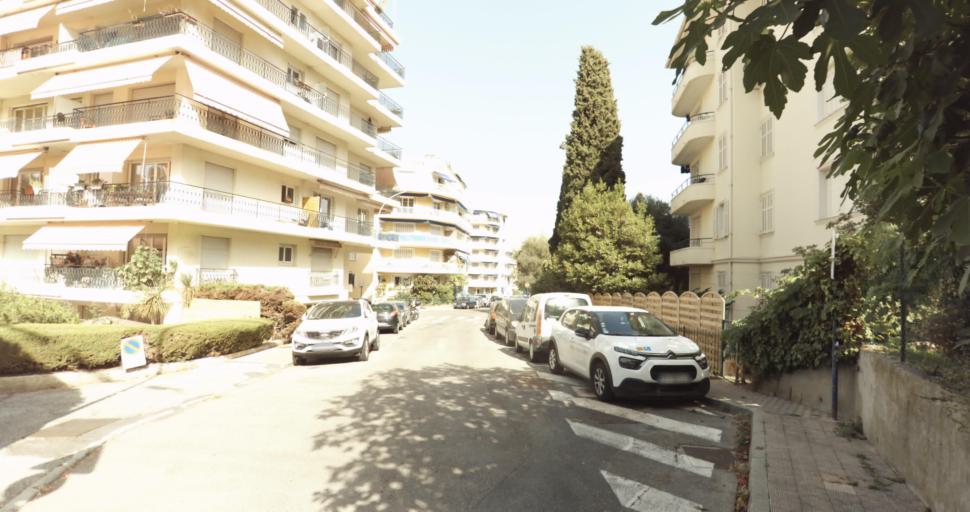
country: FR
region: Provence-Alpes-Cote d'Azur
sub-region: Departement des Alpes-Maritimes
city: Roquebrune-Cap-Martin
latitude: 43.7712
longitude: 7.4906
